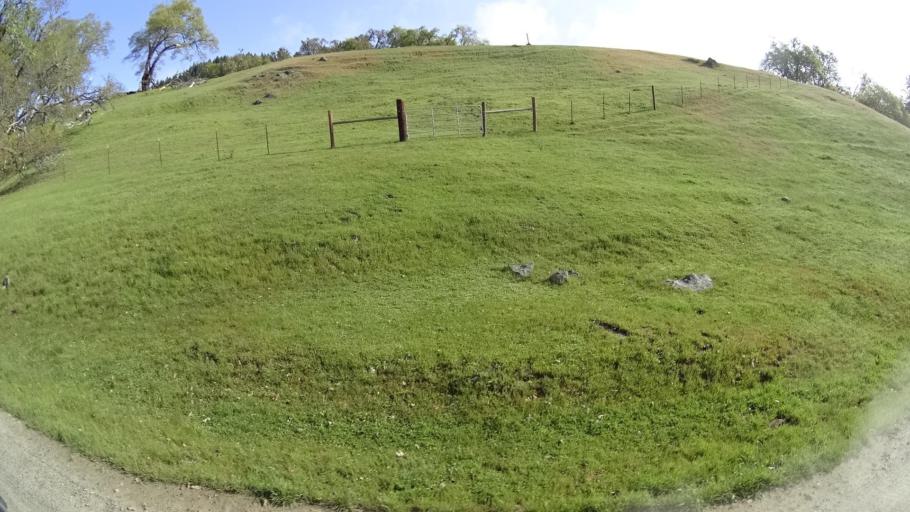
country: US
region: California
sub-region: Humboldt County
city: Hydesville
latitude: 40.6411
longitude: -123.8907
